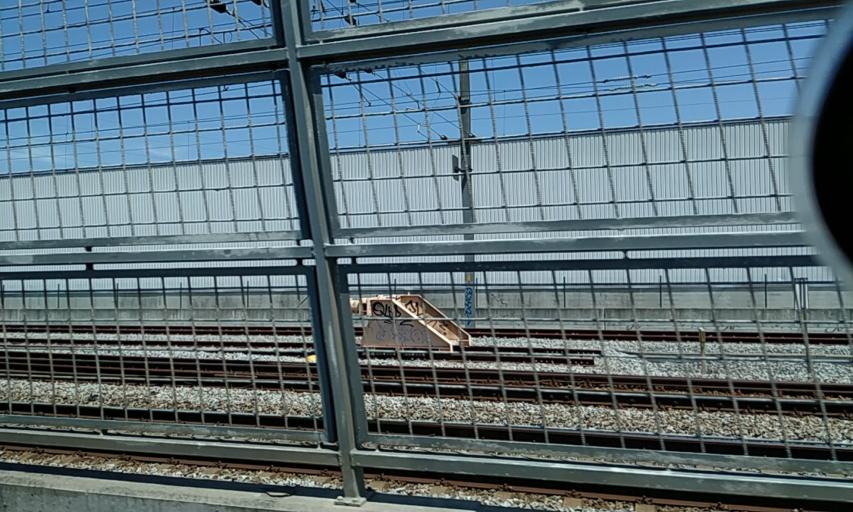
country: PT
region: Setubal
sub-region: Palmela
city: Palmela
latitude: 38.5746
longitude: -8.8735
